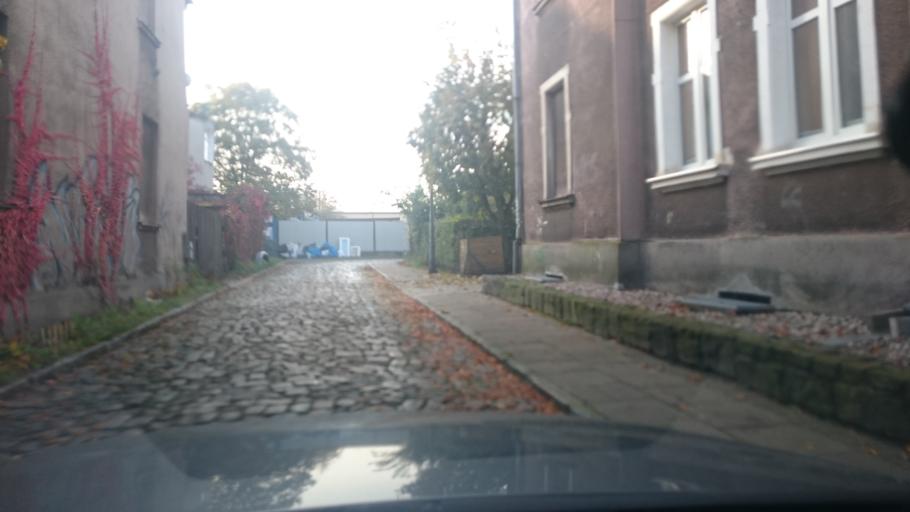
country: PL
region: Pomeranian Voivodeship
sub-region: Sopot
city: Sopot
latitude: 54.4095
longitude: 18.5707
